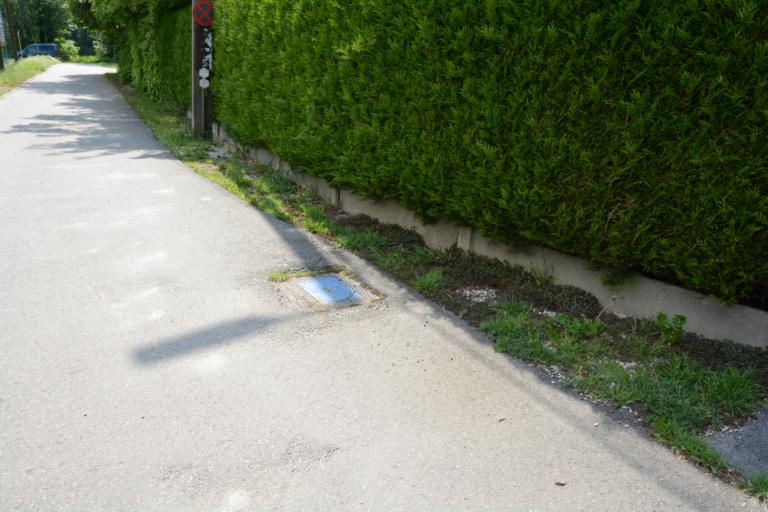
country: BE
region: Flanders
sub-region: Provincie Vlaams-Brabant
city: Boutersem
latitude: 50.8488
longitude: 4.8503
